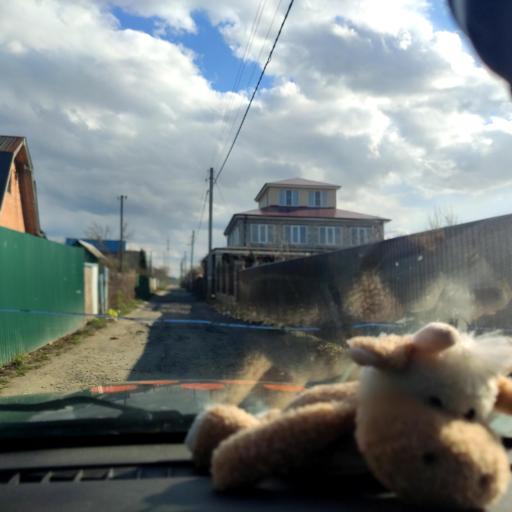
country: RU
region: Samara
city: Tol'yatti
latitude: 53.5923
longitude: 49.3083
